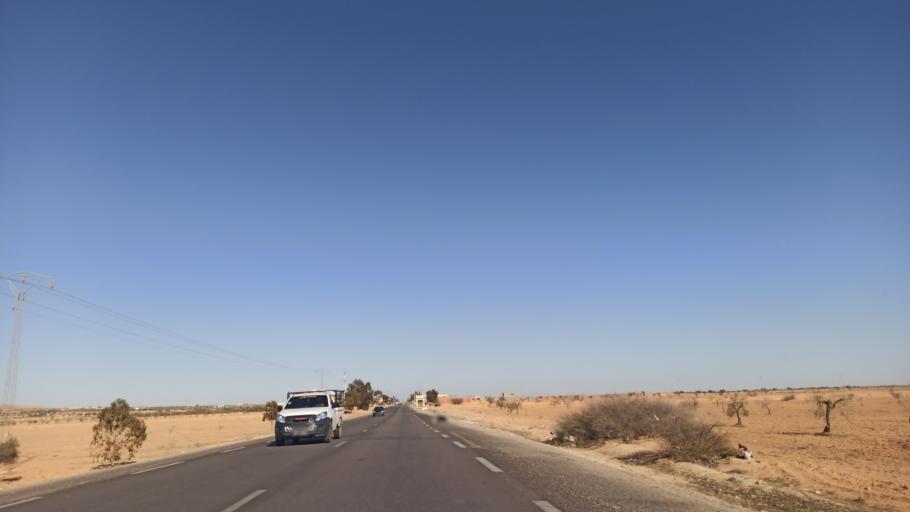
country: TN
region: Sidi Bu Zayd
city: Bi'r al Hufayy
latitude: 34.7360
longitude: 9.0704
